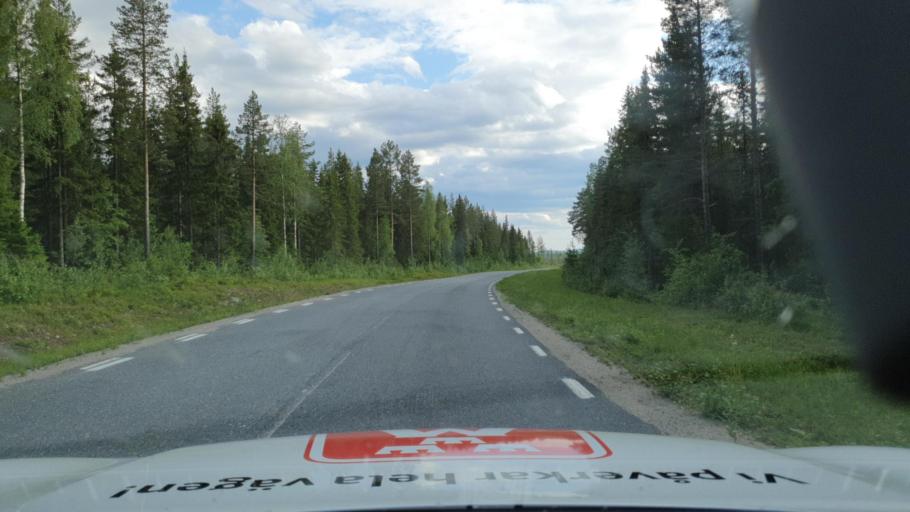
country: SE
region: Vaesterbotten
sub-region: Vindelns Kommun
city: Vindeln
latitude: 64.4777
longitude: 19.7660
